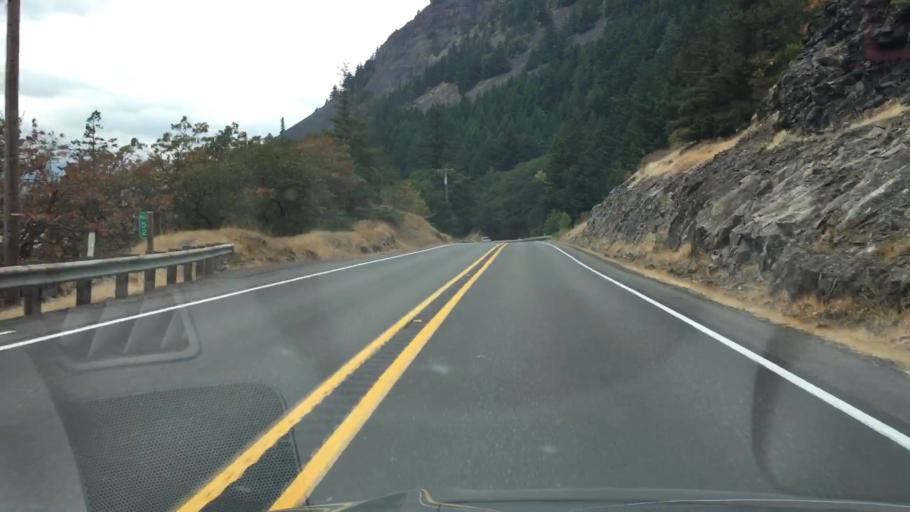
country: US
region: Washington
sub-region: Skamania County
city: Carson
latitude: 45.7017
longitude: -121.7426
